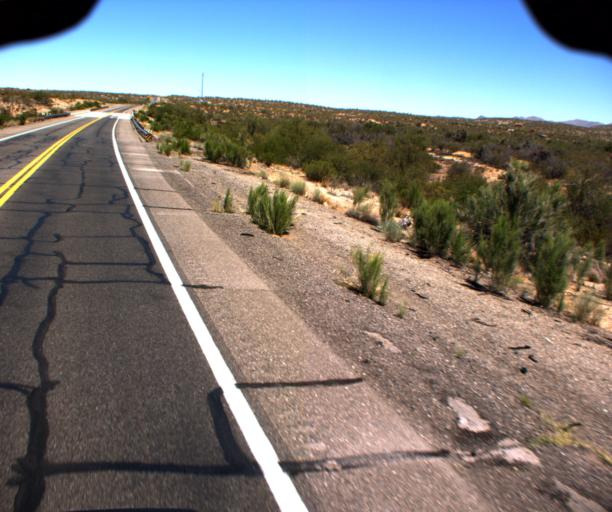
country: US
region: Arizona
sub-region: Yavapai County
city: Congress
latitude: 34.2041
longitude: -113.0634
